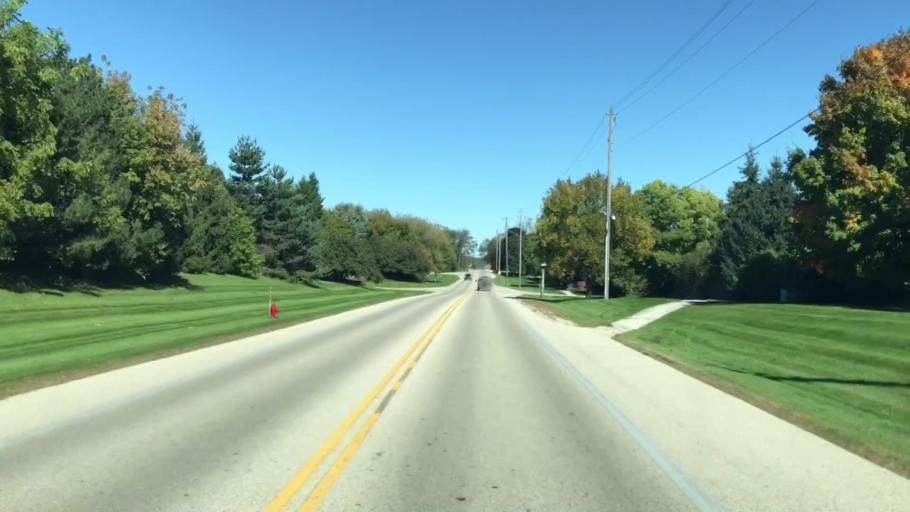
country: US
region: Wisconsin
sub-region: Waukesha County
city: Brookfield
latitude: 43.0669
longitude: -88.1662
